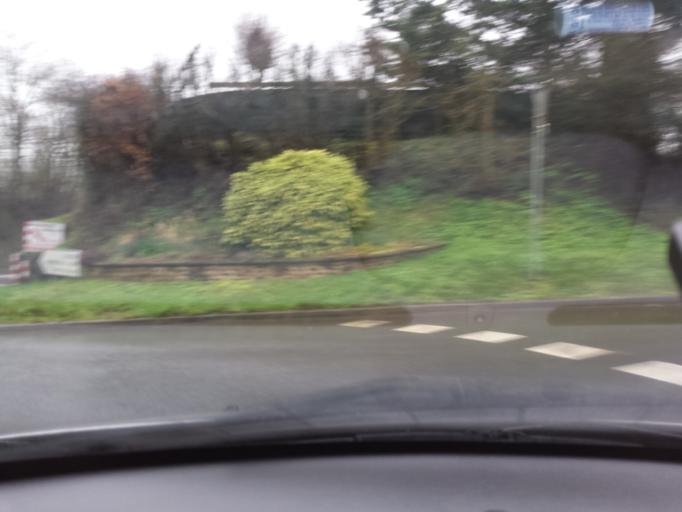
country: FR
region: Pays de la Loire
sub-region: Departement de la Vendee
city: Bournezeau
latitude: 46.5599
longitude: -1.1599
